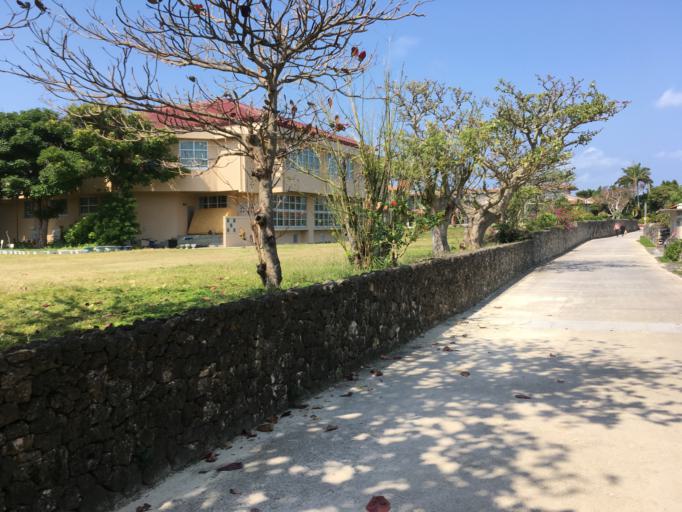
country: JP
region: Okinawa
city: Ishigaki
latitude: 24.3276
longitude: 124.0866
